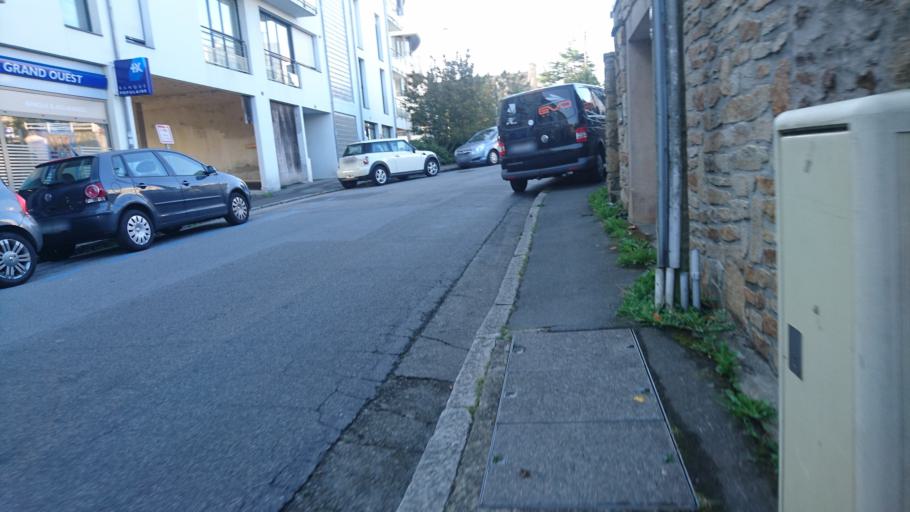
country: FR
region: Brittany
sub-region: Departement du Finistere
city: Brest
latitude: 48.3978
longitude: -4.4544
